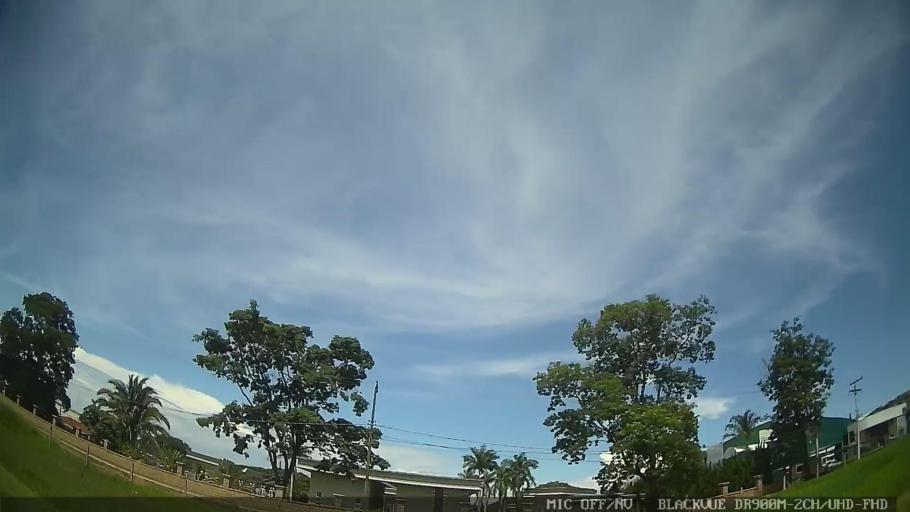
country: BR
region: Sao Paulo
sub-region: Jaguariuna
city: Jaguariuna
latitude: -22.6303
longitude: -47.0057
